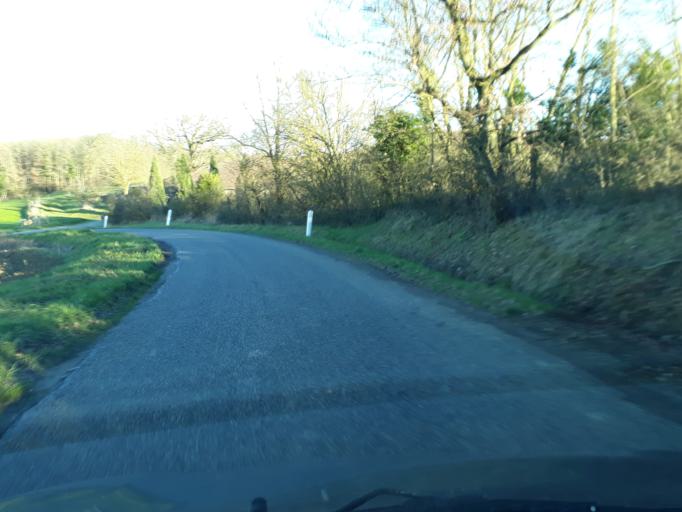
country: FR
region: Midi-Pyrenees
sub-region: Departement du Gers
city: Aubiet
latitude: 43.6400
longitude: 0.7011
